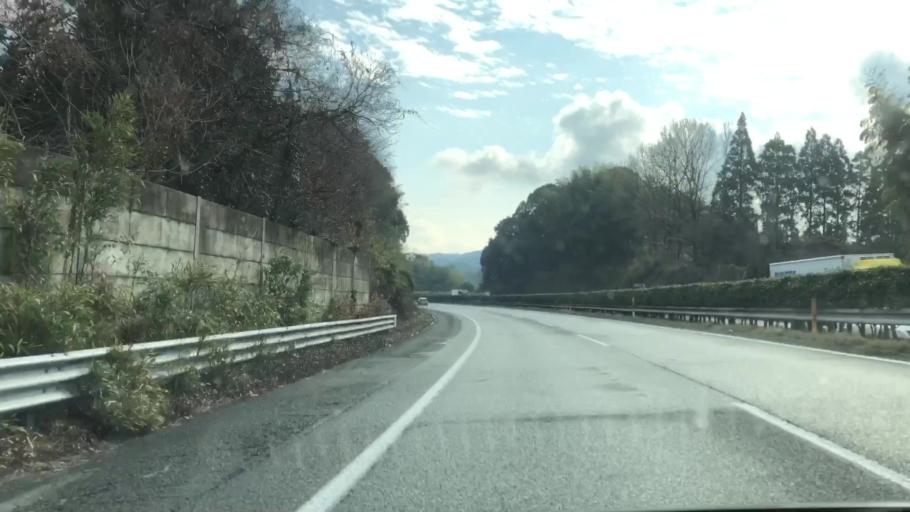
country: JP
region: Kumamoto
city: Tamana
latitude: 33.0070
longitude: 130.5828
